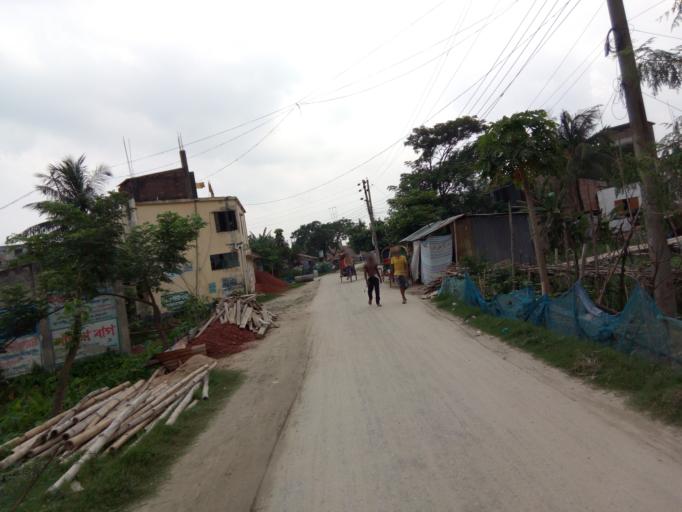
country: BD
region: Dhaka
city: Paltan
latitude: 23.7045
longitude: 90.4839
